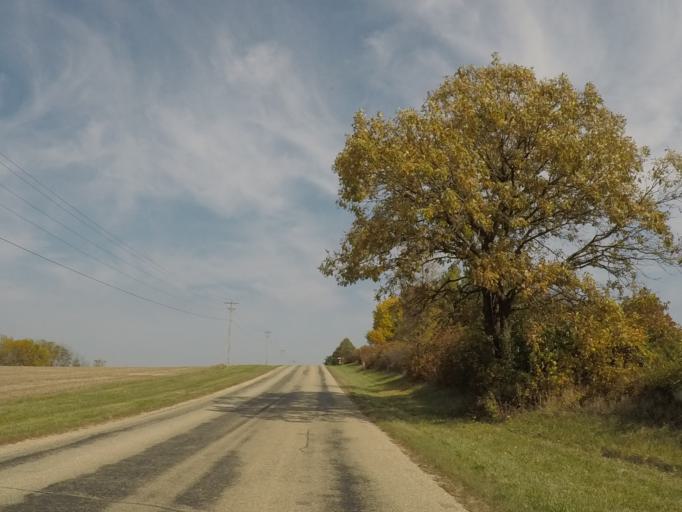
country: US
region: Wisconsin
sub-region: Dane County
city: Cross Plains
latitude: 43.0480
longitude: -89.6011
